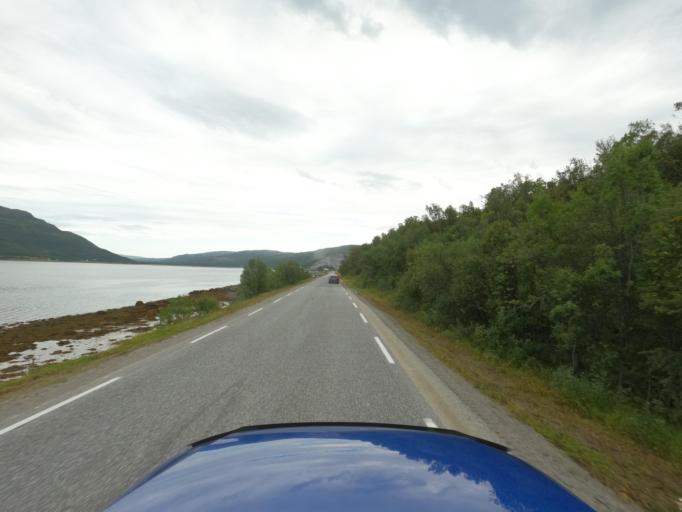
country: NO
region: Finnmark Fylke
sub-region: Kvalsund
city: Kvalsund
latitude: 70.4601
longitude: 24.2680
